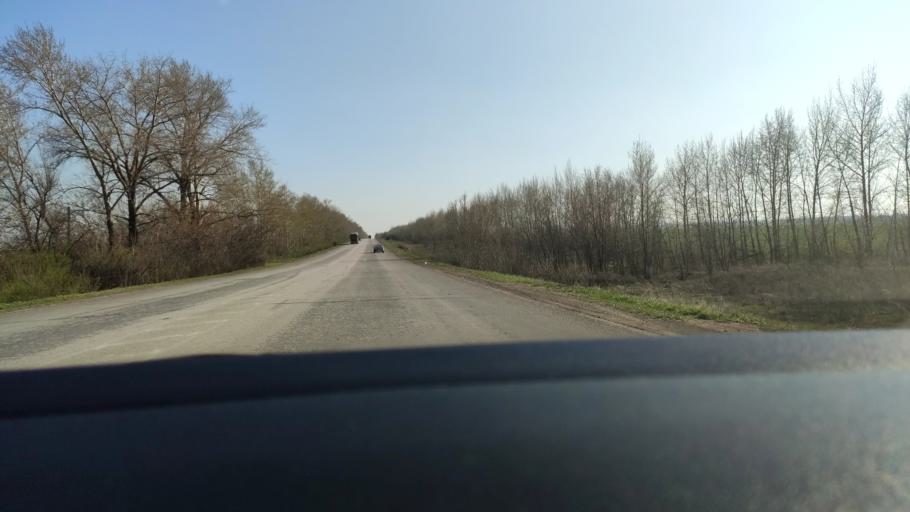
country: RU
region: Voronezj
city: Maslovka
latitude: 51.4726
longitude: 39.3059
